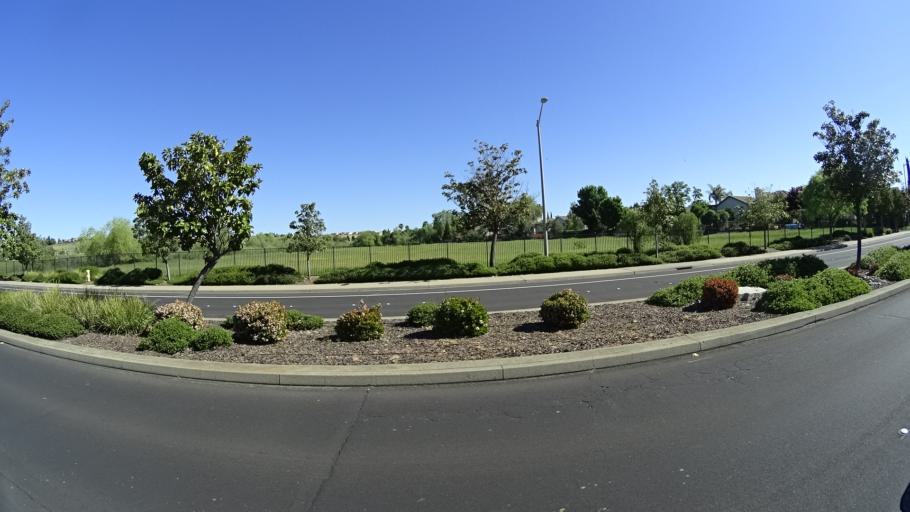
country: US
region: California
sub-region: Placer County
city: Rocklin
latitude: 38.8143
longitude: -121.2643
